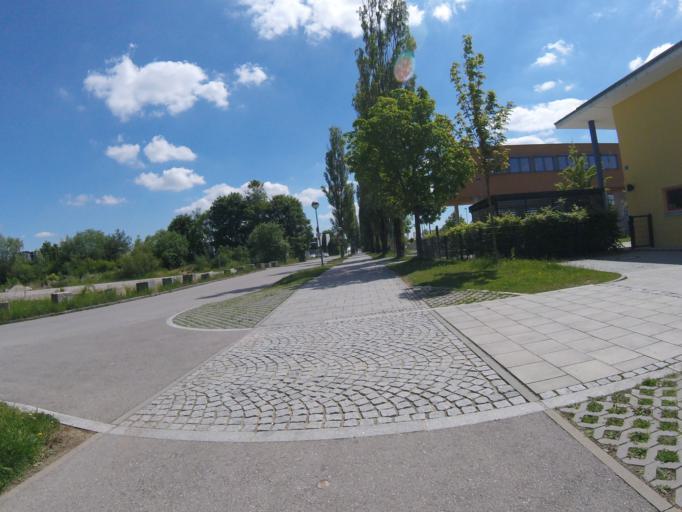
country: DE
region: Bavaria
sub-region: Upper Bavaria
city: Unterhaching
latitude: 48.0722
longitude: 11.6163
